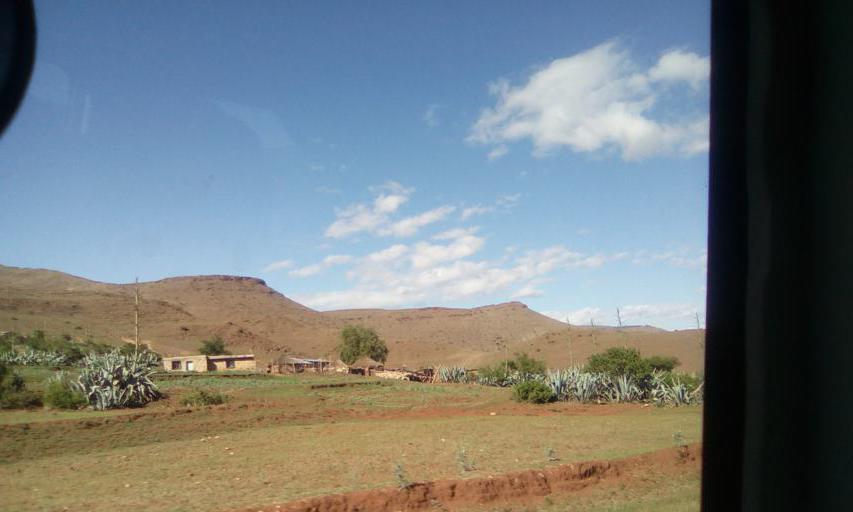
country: LS
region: Qacha's Nek
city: Qacha's Nek
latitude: -30.0465
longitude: 28.2817
